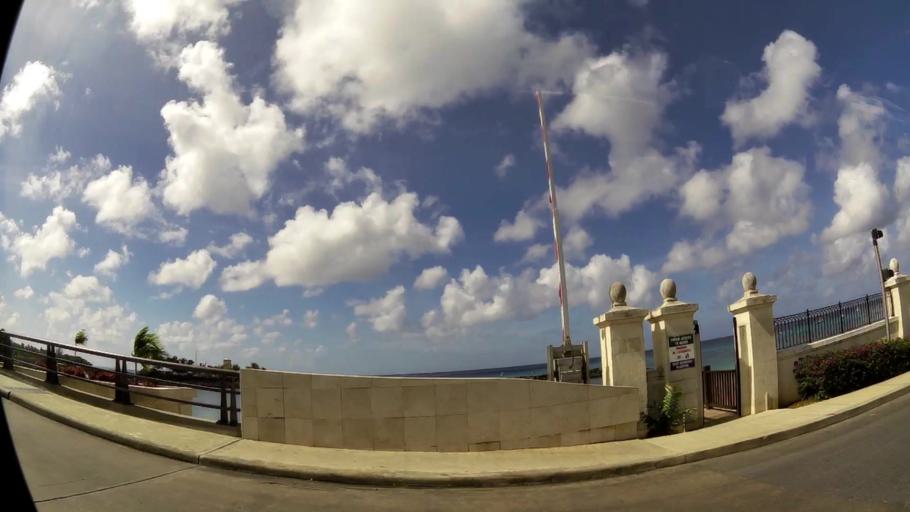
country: BB
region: Saint Peter
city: Speightstown
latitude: 13.2659
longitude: -59.6436
